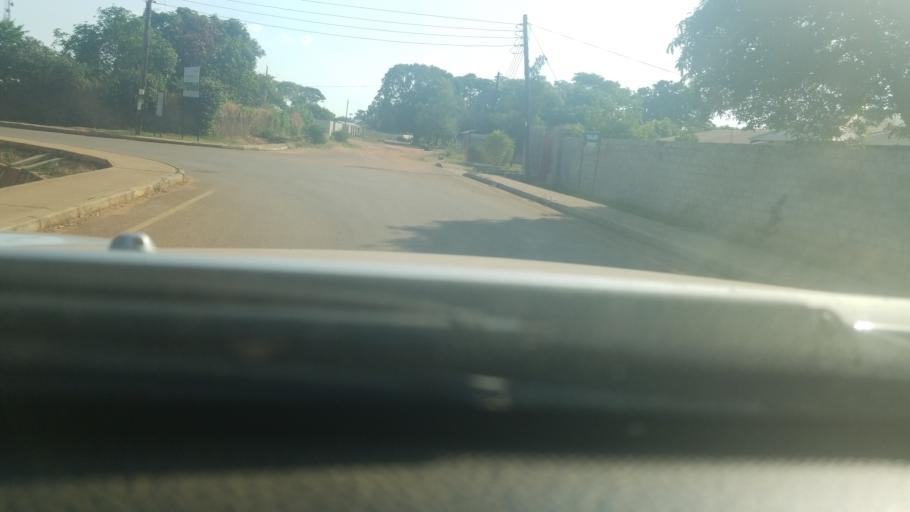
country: ZM
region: Northern
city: Kasama
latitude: -10.2010
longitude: 31.1818
